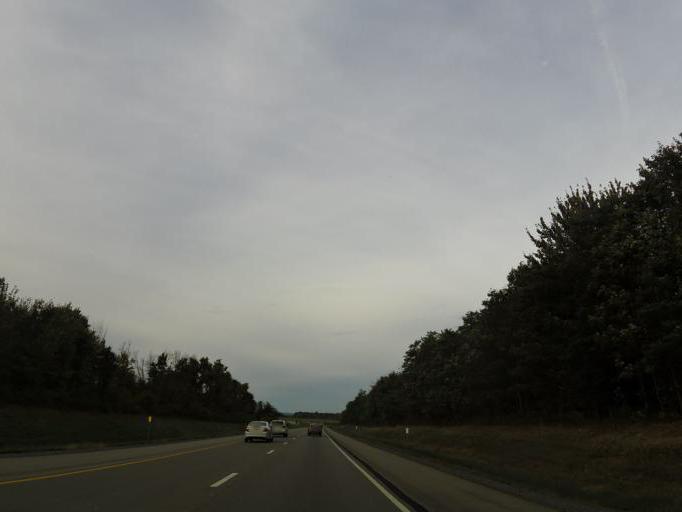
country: US
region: New York
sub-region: Erie County
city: Angola
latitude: 42.6172
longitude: -79.0119
